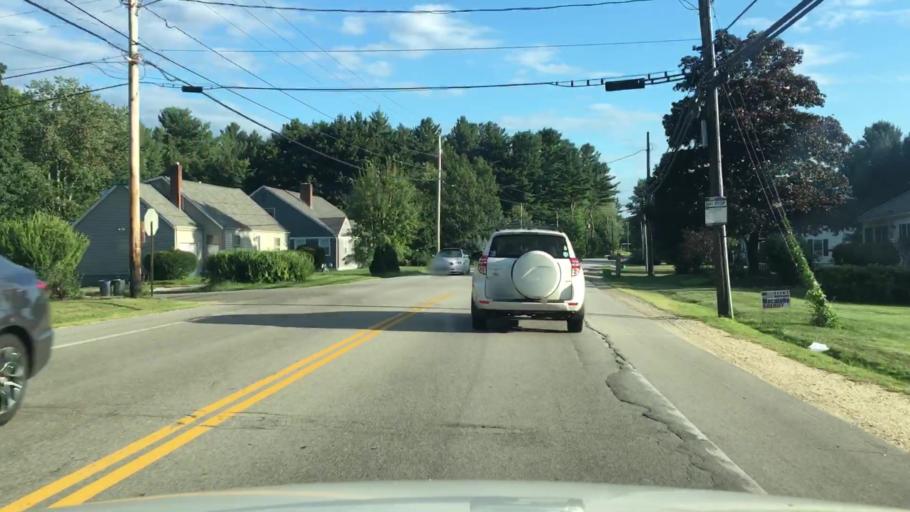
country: US
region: Maine
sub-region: York County
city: Eliot
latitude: 43.1449
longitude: -70.8384
